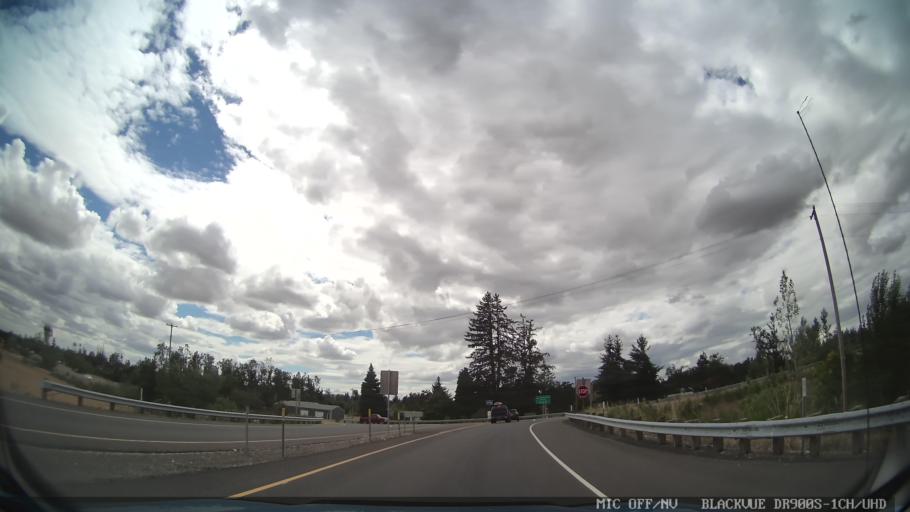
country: US
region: Oregon
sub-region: Marion County
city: Aumsville
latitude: 44.8504
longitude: -122.8650
